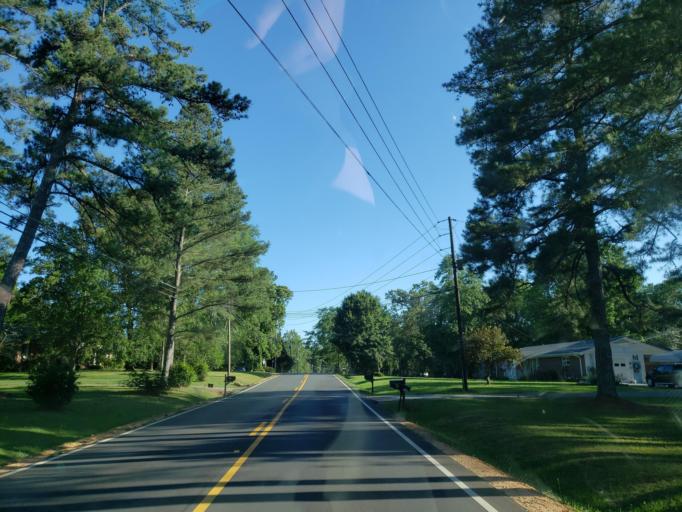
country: US
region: Georgia
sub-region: Floyd County
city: Rome
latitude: 34.3322
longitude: -85.1598
